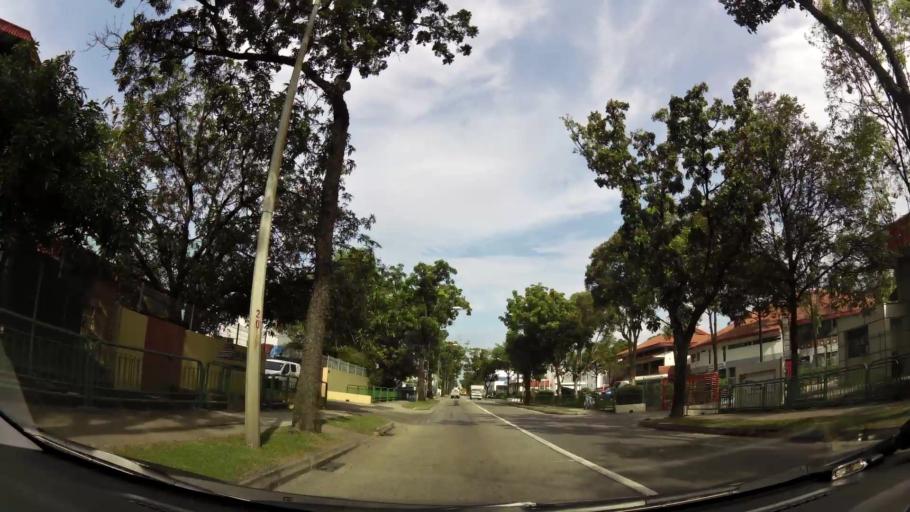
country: MY
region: Johor
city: Johor Bahru
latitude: 1.3164
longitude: 103.6524
